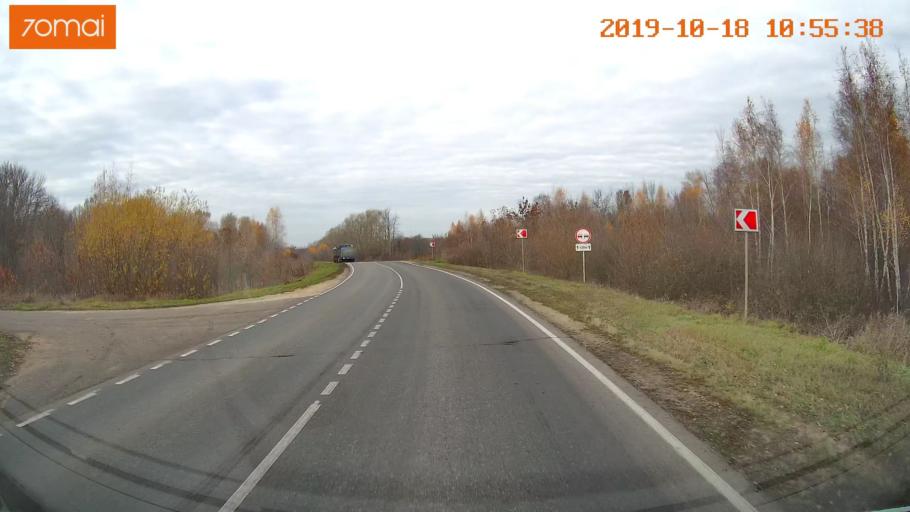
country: RU
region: Tula
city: Yepifan'
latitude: 53.8020
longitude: 38.5948
